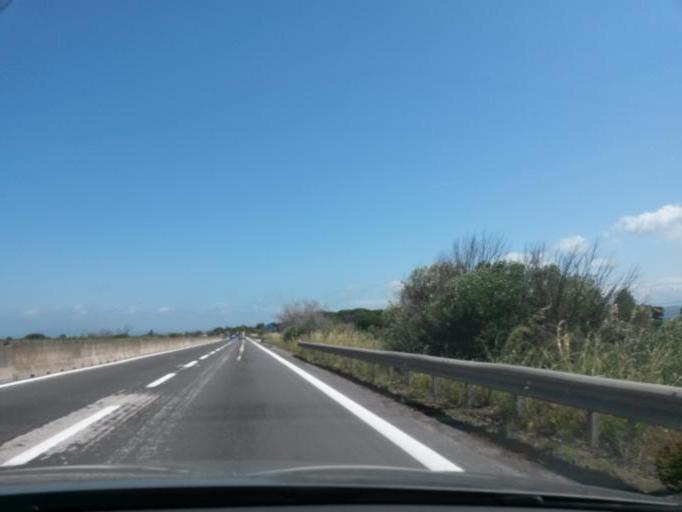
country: IT
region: Tuscany
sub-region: Provincia di Livorno
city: Donoratico
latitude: 43.1602
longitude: 10.5595
